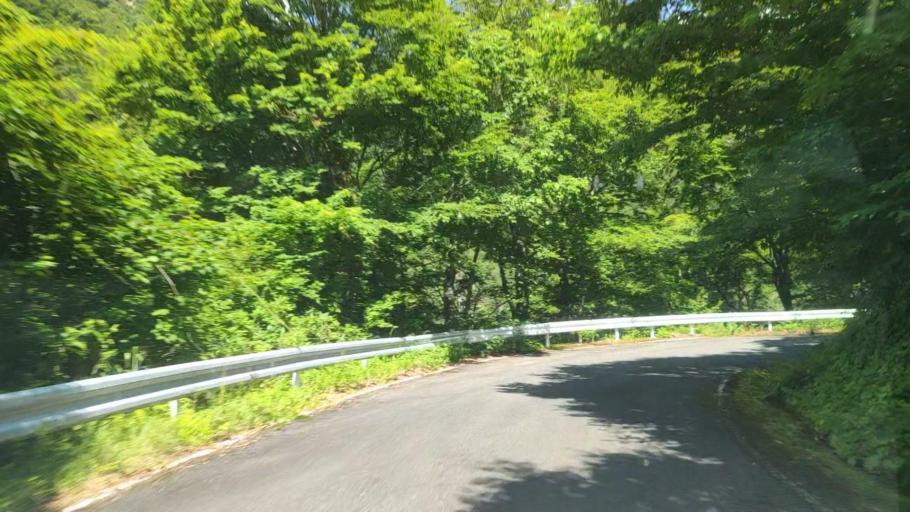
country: JP
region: Fukui
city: Ono
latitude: 35.7725
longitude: 136.5313
